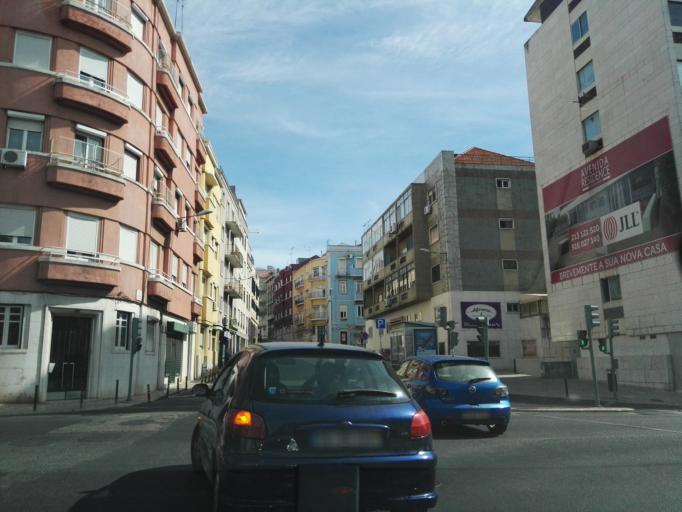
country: PT
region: Setubal
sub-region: Almada
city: Cacilhas
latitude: 38.7116
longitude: -9.1641
